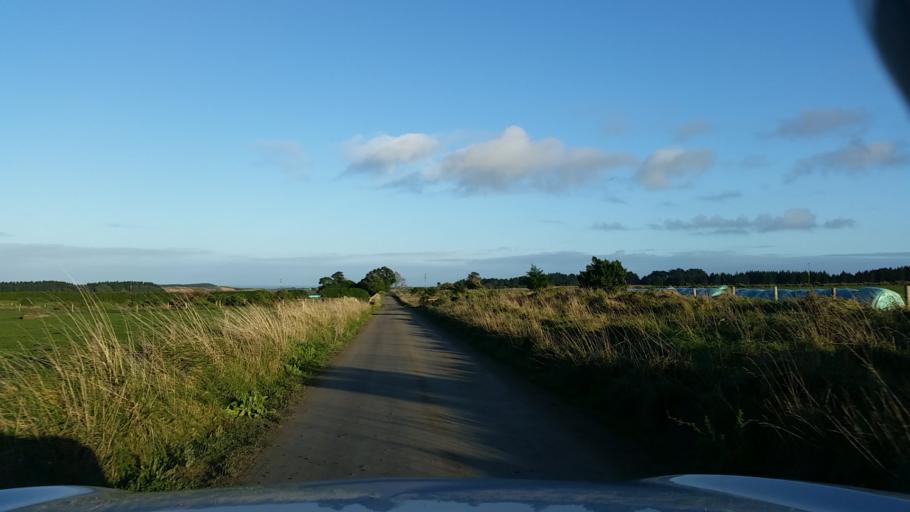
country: NZ
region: Manawatu-Wanganui
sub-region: Wanganui District
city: Wanganui
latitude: -39.8203
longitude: 174.7980
